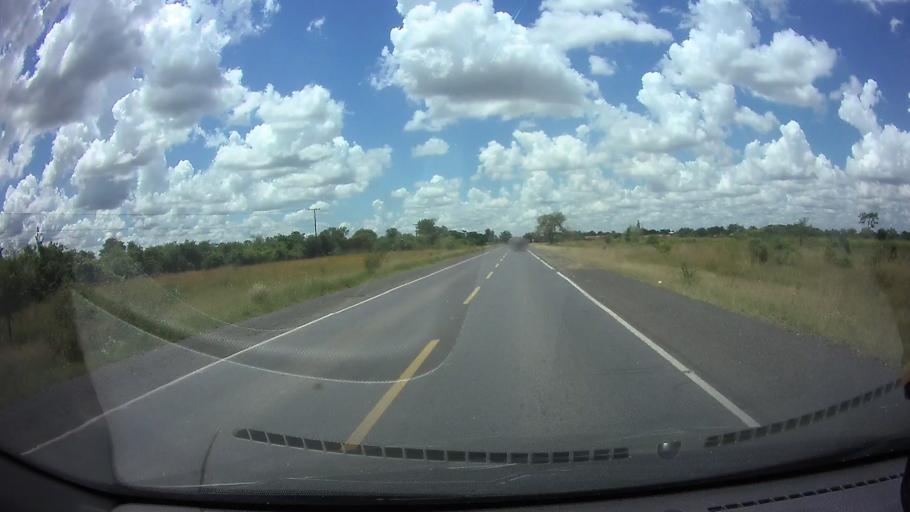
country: PY
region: Presidente Hayes
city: Nanawa
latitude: -25.2211
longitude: -57.6775
